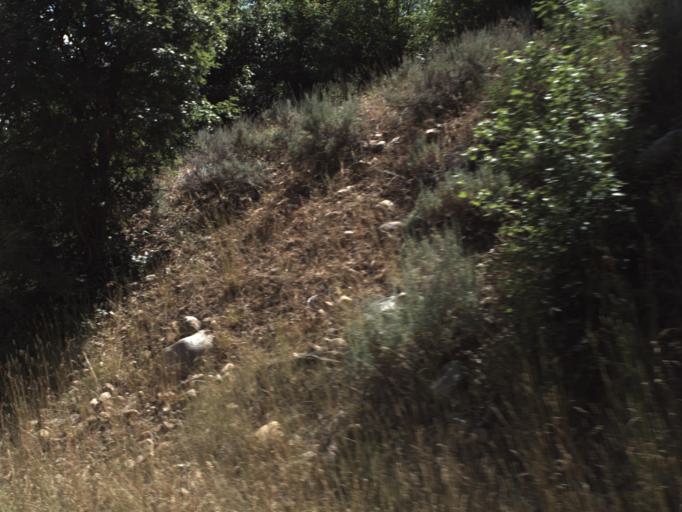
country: US
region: Utah
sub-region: Weber County
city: Wolf Creek
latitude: 41.3253
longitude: -111.6163
